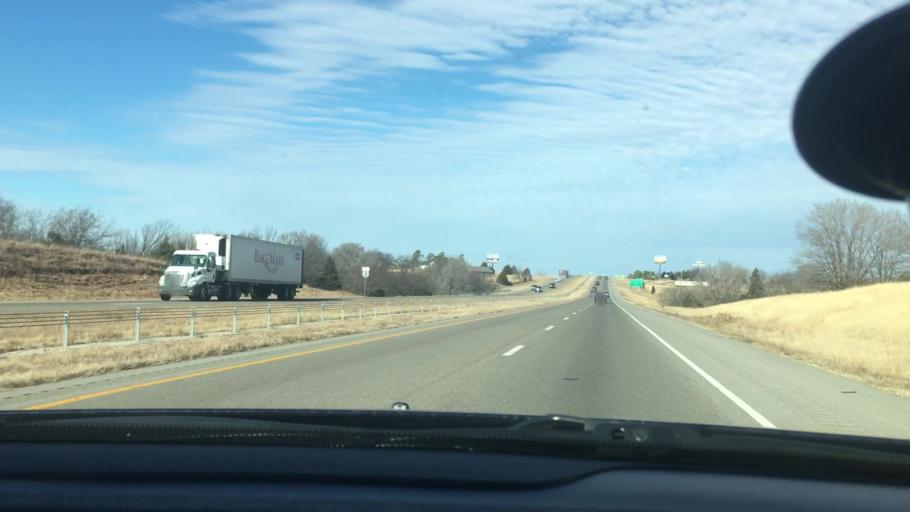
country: US
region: Oklahoma
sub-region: Cleveland County
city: Noble
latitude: 35.0731
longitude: -97.4019
